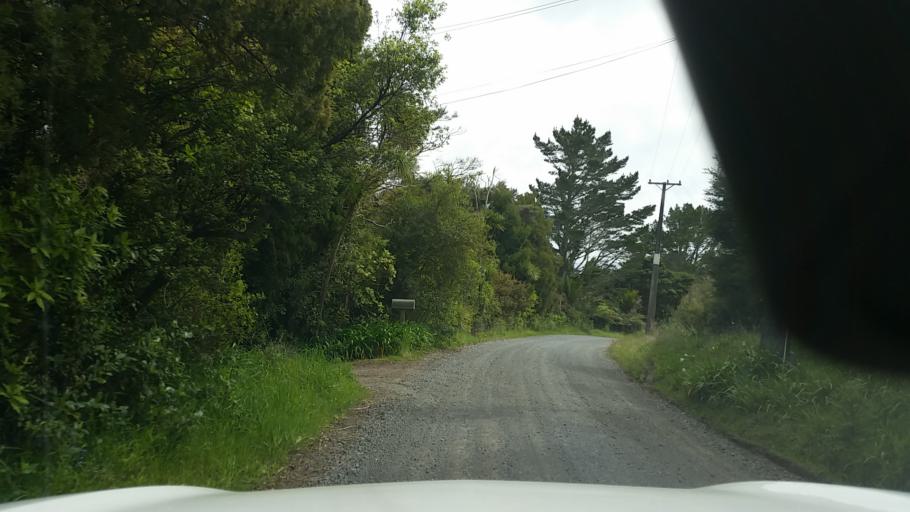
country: NZ
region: Auckland
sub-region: Auckland
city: Muriwai Beach
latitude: -36.8479
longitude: 174.5100
